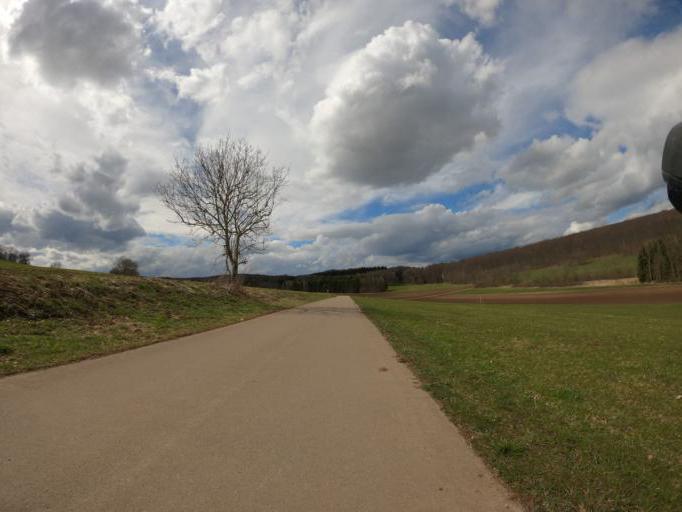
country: DE
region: Baden-Wuerttemberg
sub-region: Tuebingen Region
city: Pfullingen
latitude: 48.4004
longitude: 9.1676
